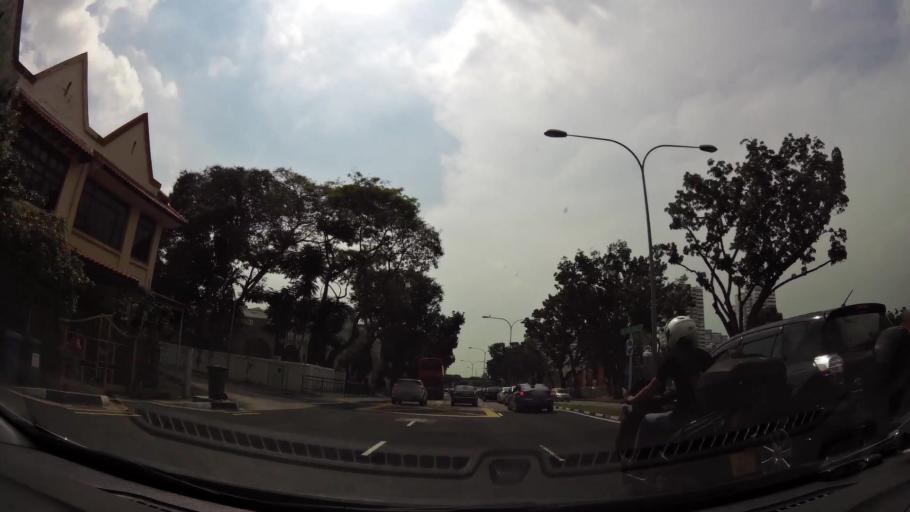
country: SG
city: Singapore
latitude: 1.3074
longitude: 103.9090
